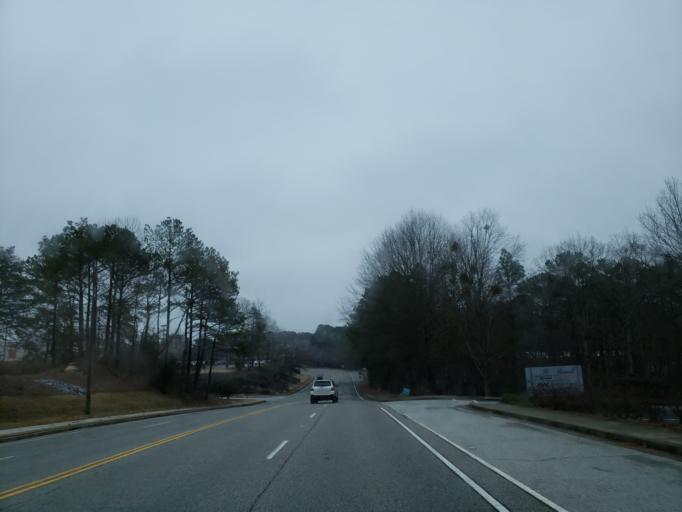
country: US
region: Georgia
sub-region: Fulton County
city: Roswell
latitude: 34.0162
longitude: -84.3214
